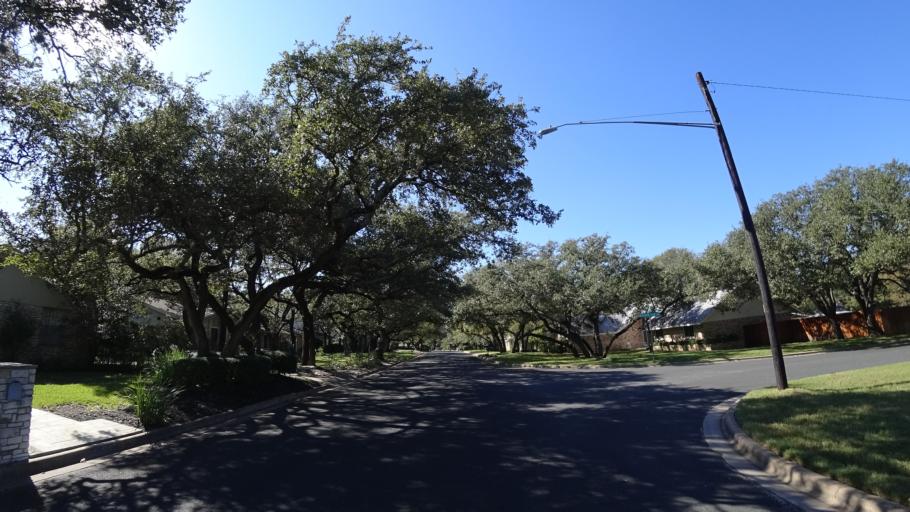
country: US
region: Texas
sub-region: Williamson County
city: Jollyville
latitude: 30.3824
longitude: -97.7497
